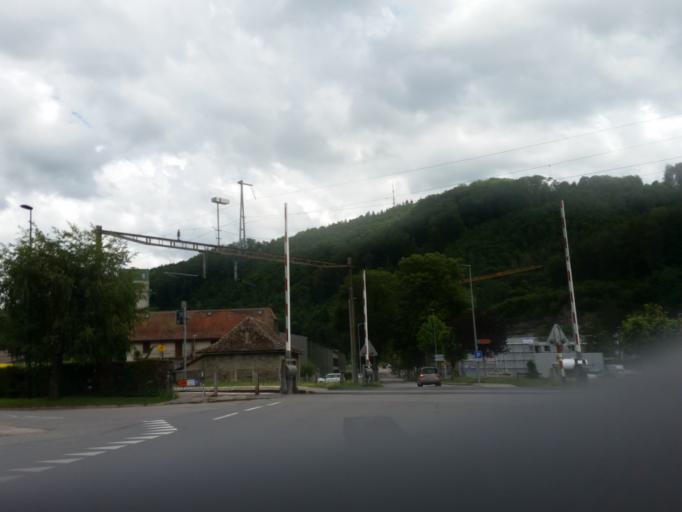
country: CH
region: Vaud
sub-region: Broye-Vully District
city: Moudon
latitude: 46.6674
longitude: 6.8013
